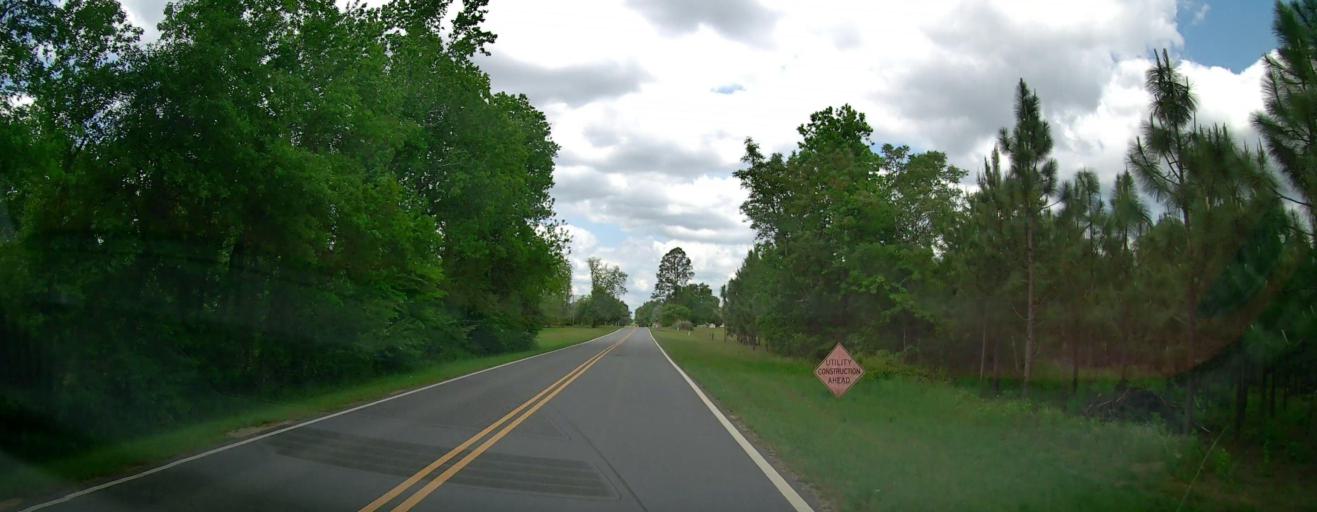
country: US
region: Georgia
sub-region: Laurens County
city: Dublin
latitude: 32.6055
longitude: -82.9611
